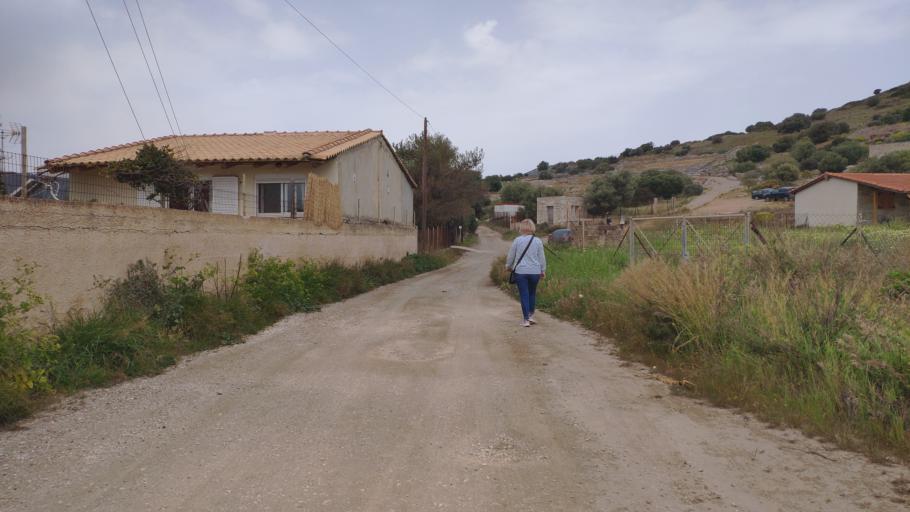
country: GR
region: Attica
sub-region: Nomarchia Anatolikis Attikis
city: Lavrio
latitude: 37.7360
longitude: 24.0545
